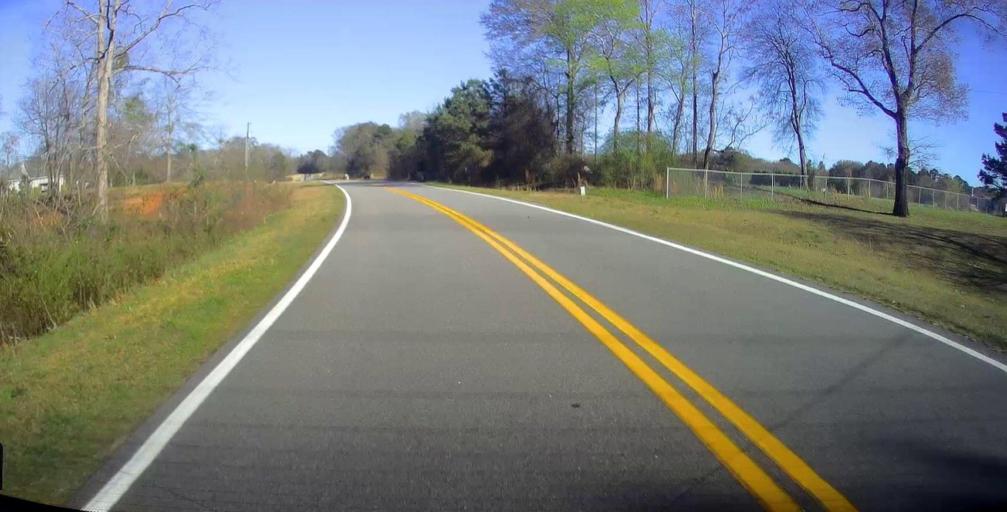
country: US
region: Georgia
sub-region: Peach County
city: Byron
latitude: 32.6735
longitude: -83.8283
